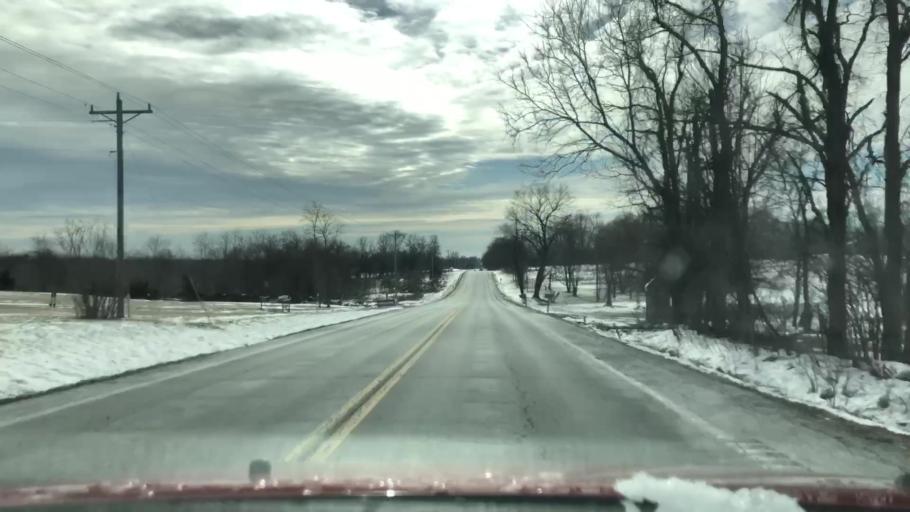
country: US
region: Missouri
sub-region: Jackson County
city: Lone Jack
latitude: 38.8808
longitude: -94.1350
